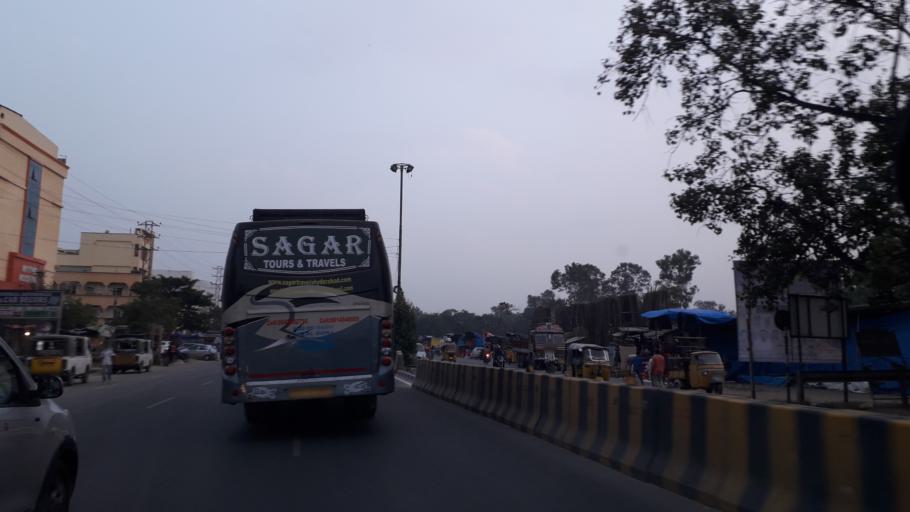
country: IN
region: Telangana
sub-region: Medak
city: Serilingampalle
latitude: 17.4987
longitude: 78.3139
